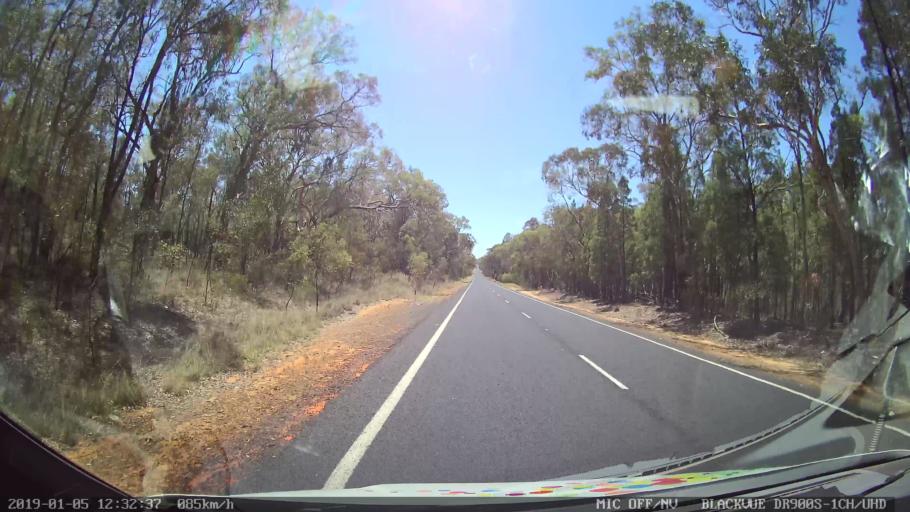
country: AU
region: New South Wales
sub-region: Warrumbungle Shire
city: Coonabarabran
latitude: -31.2168
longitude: 149.3823
